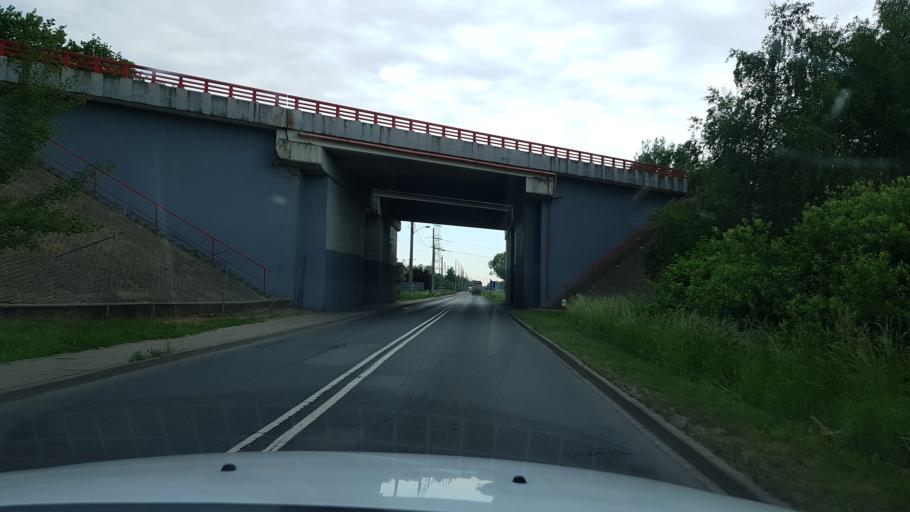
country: PL
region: West Pomeranian Voivodeship
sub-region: Powiat policki
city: Przeclaw
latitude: 53.3344
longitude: 14.5453
